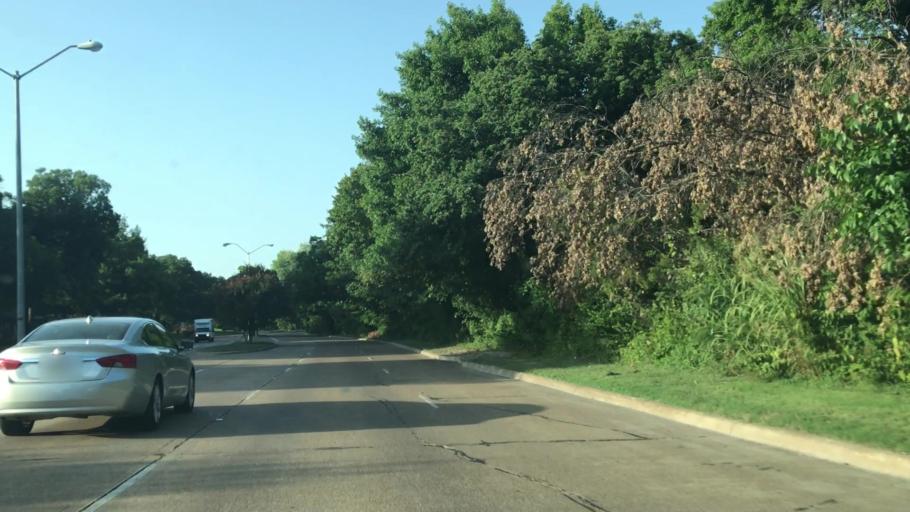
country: US
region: Texas
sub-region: Dallas County
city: Highland Park
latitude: 32.8462
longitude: -96.7042
